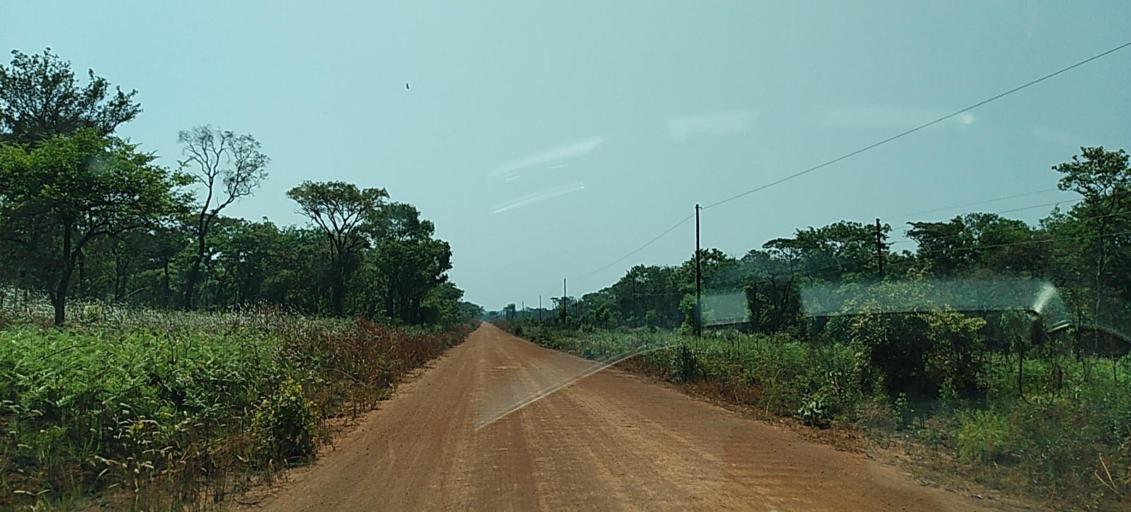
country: ZM
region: North-Western
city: Kansanshi
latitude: -11.9950
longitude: 26.6493
